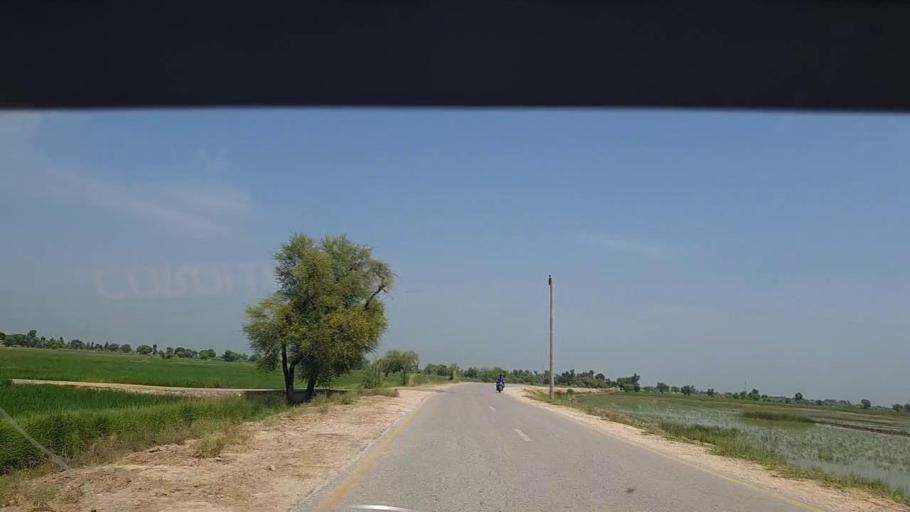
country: PK
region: Sindh
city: Rustam jo Goth
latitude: 28.1056
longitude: 68.8044
